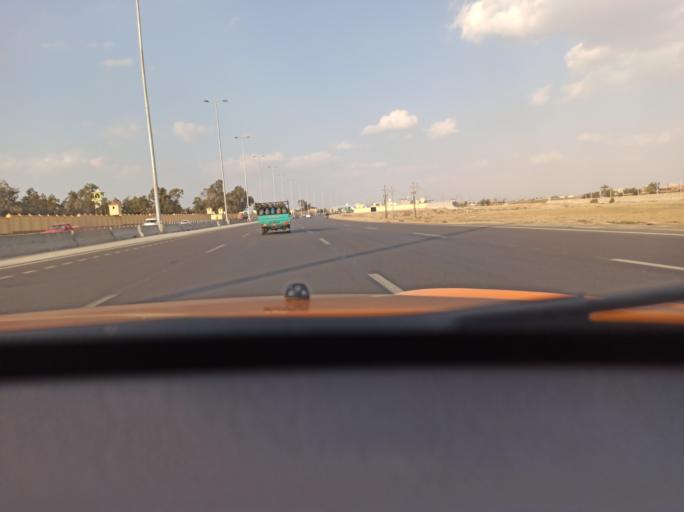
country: EG
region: Al Isma'iliyah
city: Ismailia
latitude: 30.6134
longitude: 32.2221
